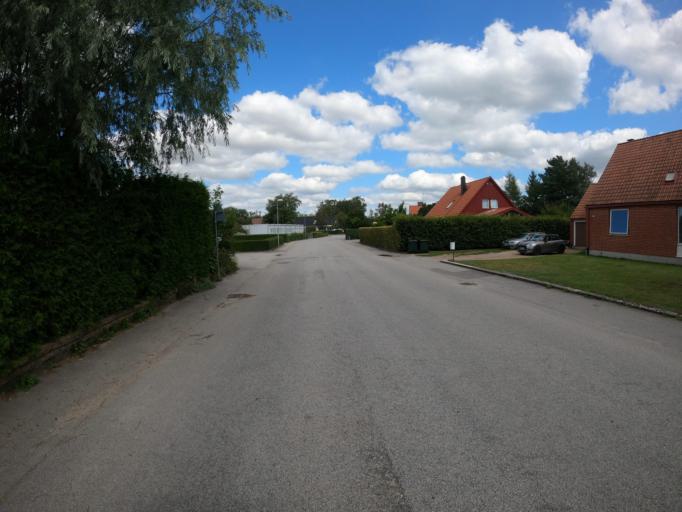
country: SE
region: Skane
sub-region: Lunds Kommun
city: Genarp
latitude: 55.5980
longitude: 13.3995
